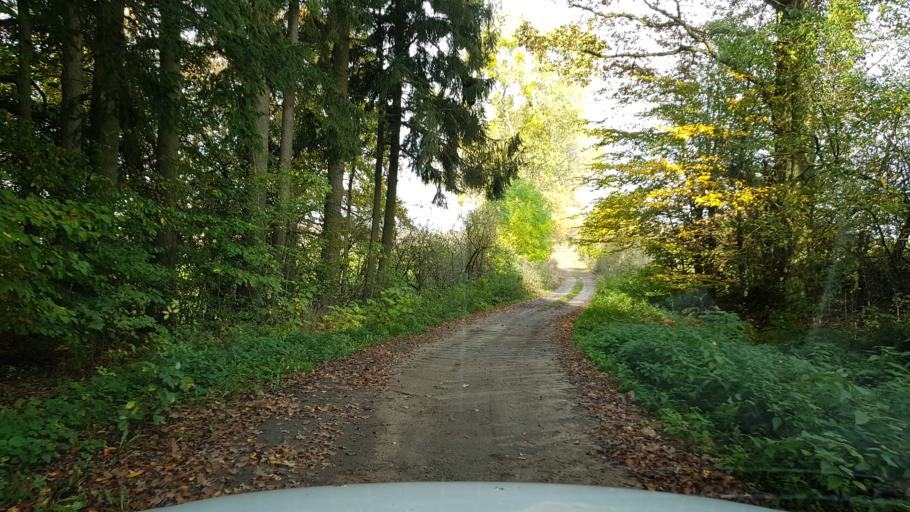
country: PL
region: West Pomeranian Voivodeship
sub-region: Powiat swidwinski
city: Polczyn-Zdroj
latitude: 53.7585
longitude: 16.0304
